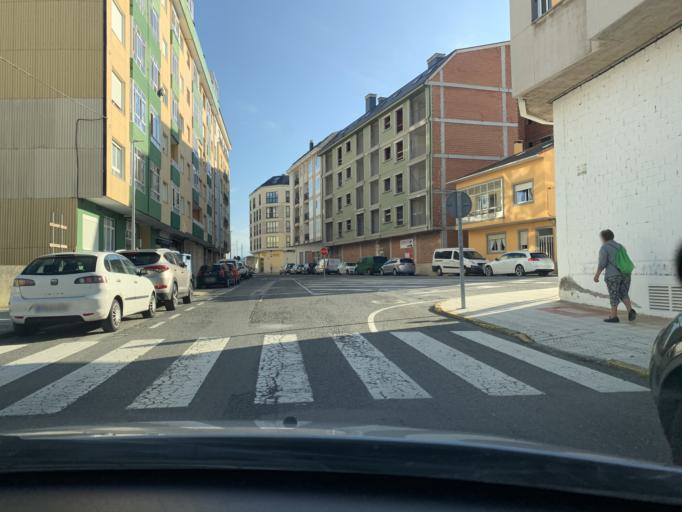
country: ES
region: Galicia
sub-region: Provincia de Lugo
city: Foz
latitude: 43.5720
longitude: -7.2521
